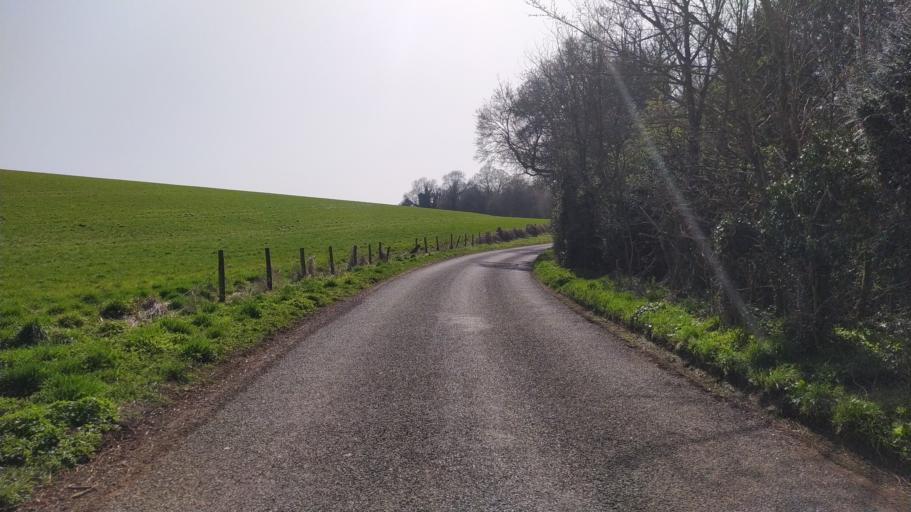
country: GB
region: England
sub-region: Hampshire
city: Kings Worthy
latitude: 51.0831
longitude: -1.2443
